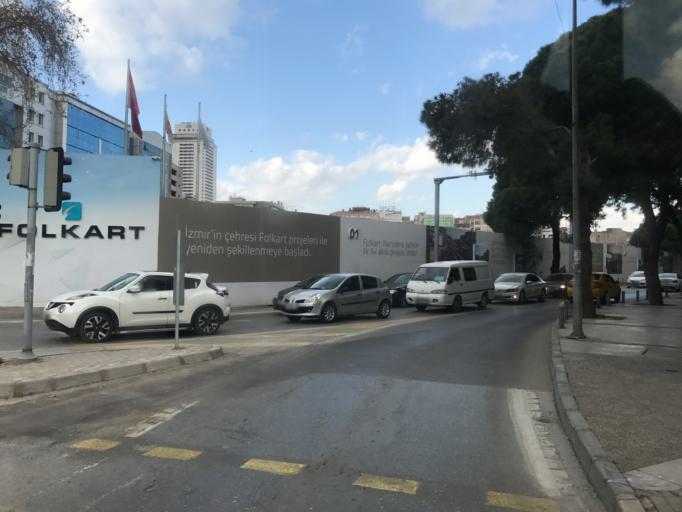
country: TR
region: Izmir
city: Izmir
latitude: 38.4242
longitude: 27.1429
